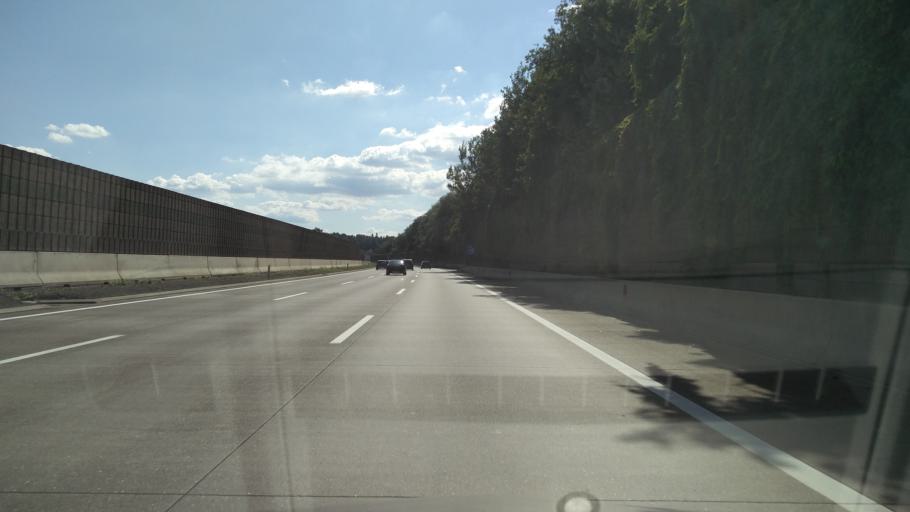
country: AT
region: Styria
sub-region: Politischer Bezirk Weiz
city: Ungerdorf
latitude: 47.0852
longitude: 15.6536
